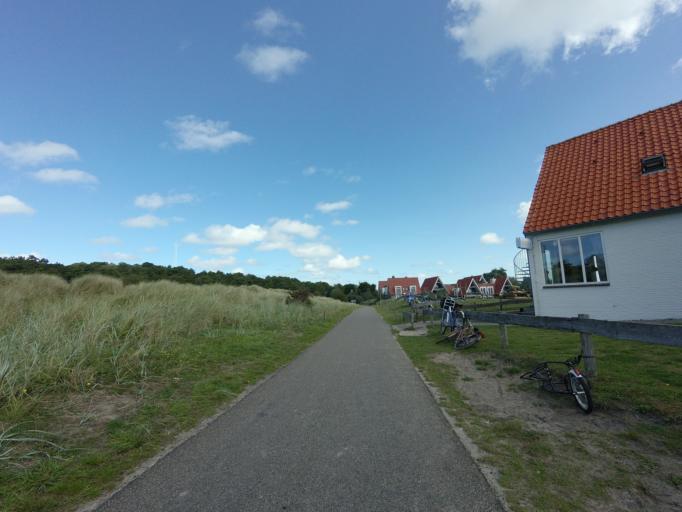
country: NL
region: Friesland
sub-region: Gemeente Terschelling
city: West-Terschelling
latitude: 53.3668
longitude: 5.2296
